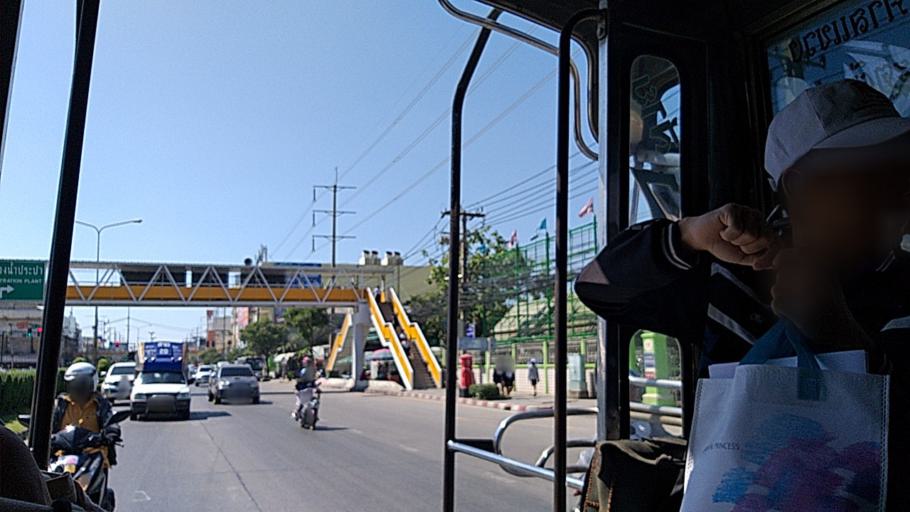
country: TH
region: Nakhon Ratchasima
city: Nakhon Ratchasima
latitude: 14.9800
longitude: 102.0989
